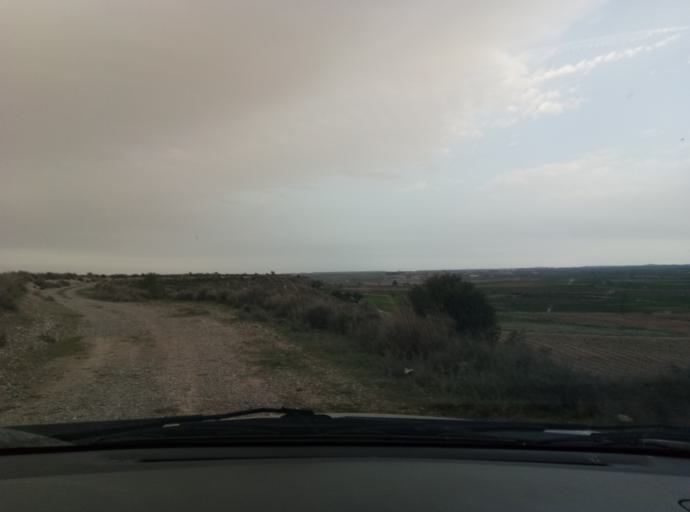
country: ES
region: Catalonia
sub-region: Provincia de Lleida
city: Verdu
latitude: 41.6097
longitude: 1.0963
